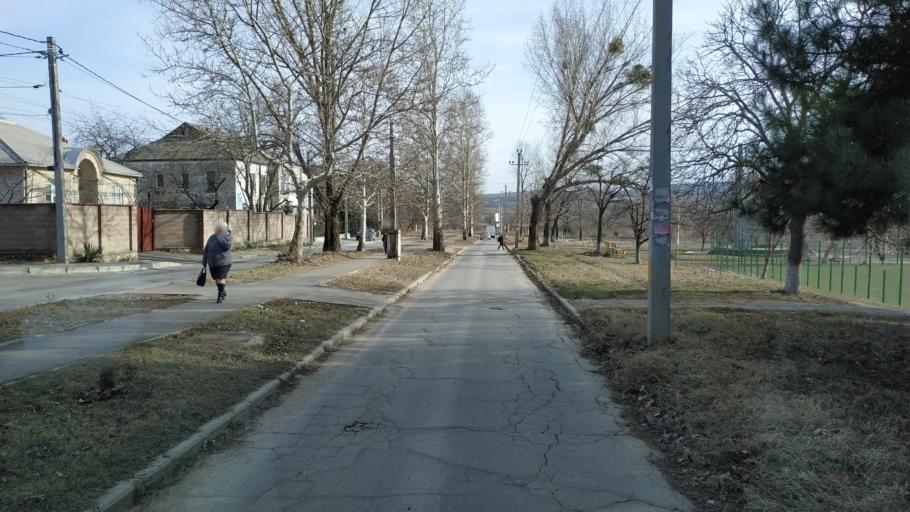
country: MD
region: Chisinau
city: Vatra
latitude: 47.0736
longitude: 28.6937
